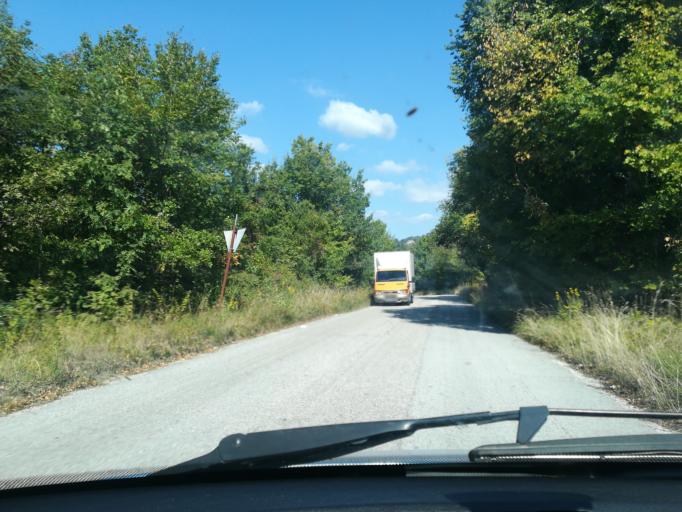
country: IT
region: The Marches
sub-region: Provincia di Macerata
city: Caldarola
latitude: 43.1492
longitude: 13.2243
